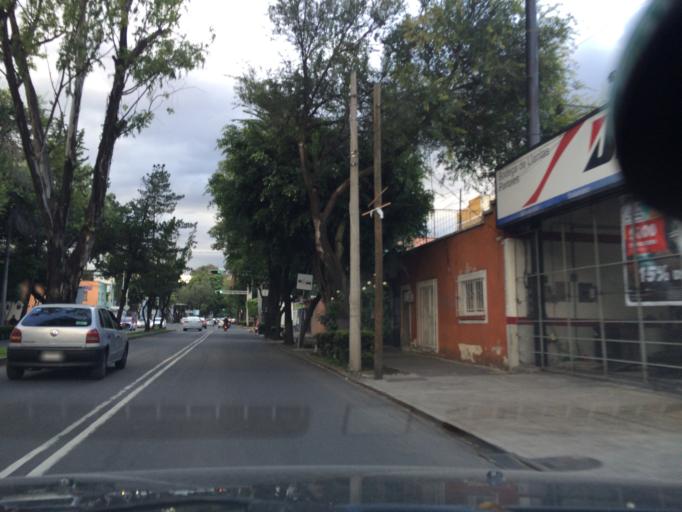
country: MX
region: Mexico City
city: Colonia Nativitas
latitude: 19.3653
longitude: -99.1483
